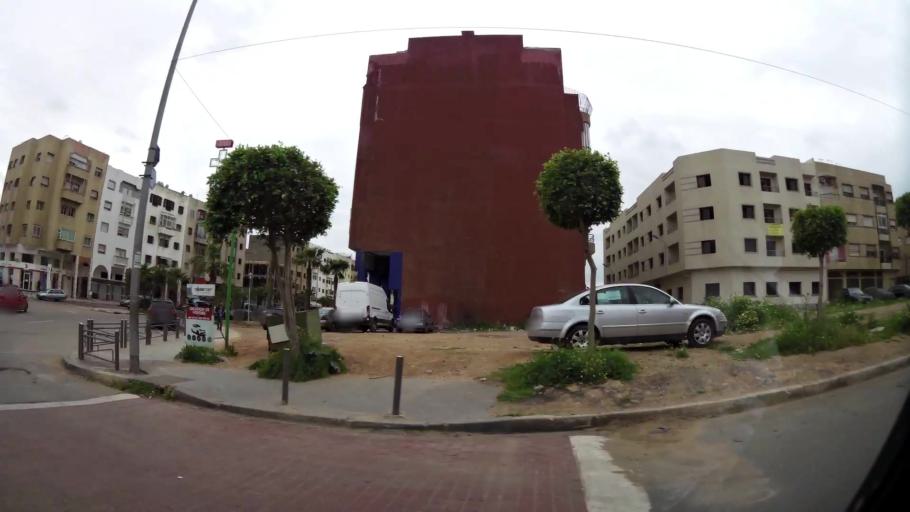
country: MA
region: Grand Casablanca
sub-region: Mediouna
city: Tit Mellil
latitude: 33.5690
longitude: -7.5477
